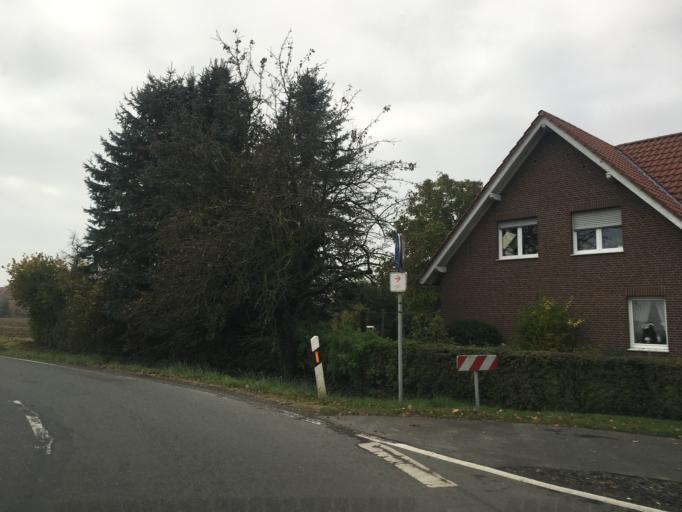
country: DE
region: North Rhine-Westphalia
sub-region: Regierungsbezirk Munster
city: Laer
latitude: 52.0195
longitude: 7.3729
